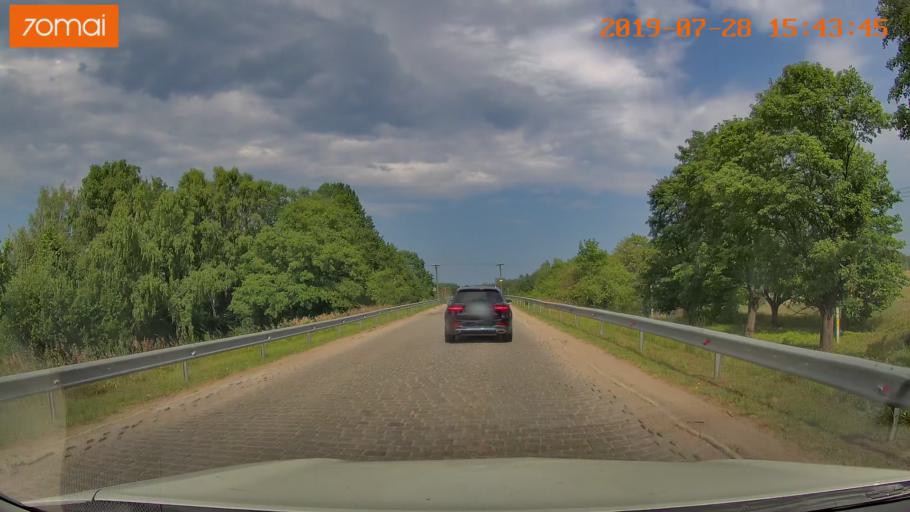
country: RU
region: Kaliningrad
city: Donskoye
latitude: 54.9382
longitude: 20.0267
